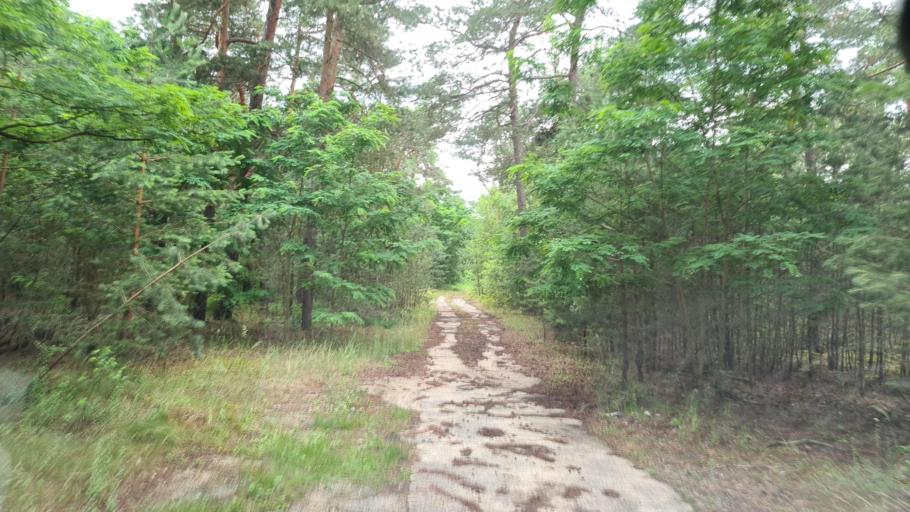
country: DE
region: Brandenburg
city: Crinitz
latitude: 51.7172
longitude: 13.7369
